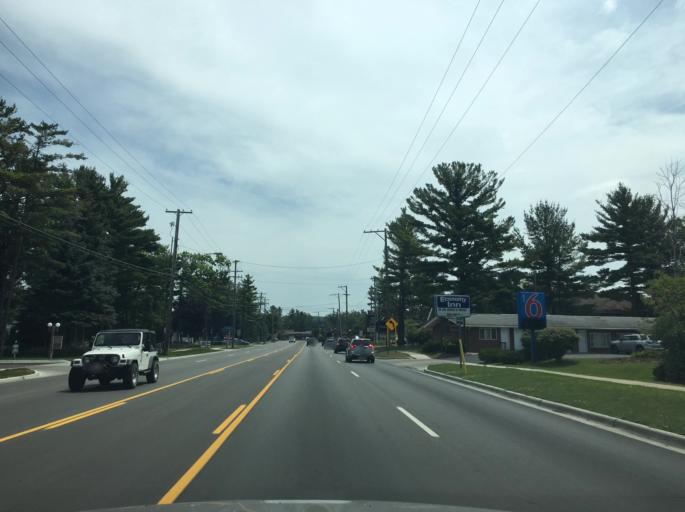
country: US
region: Michigan
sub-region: Grand Traverse County
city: Traverse City
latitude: 44.7462
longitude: -85.5449
